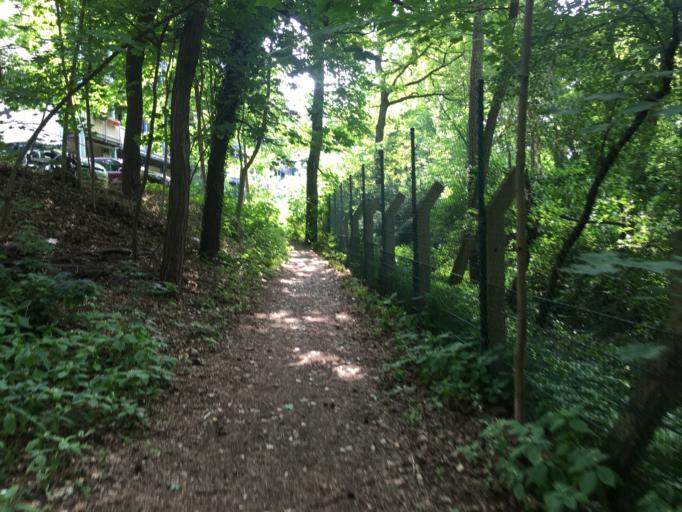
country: DE
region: Saxony
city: Albertstadt
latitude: 51.0704
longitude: 13.7713
